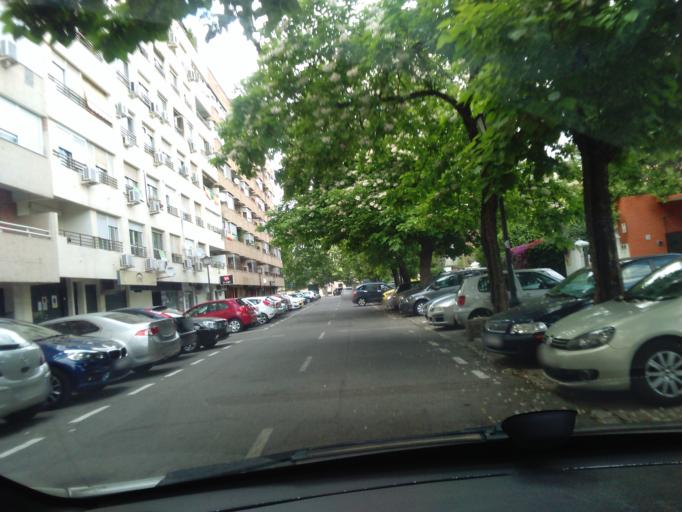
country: ES
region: Andalusia
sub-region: Provincia de Sevilla
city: Sevilla
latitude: 37.3625
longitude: -5.9854
